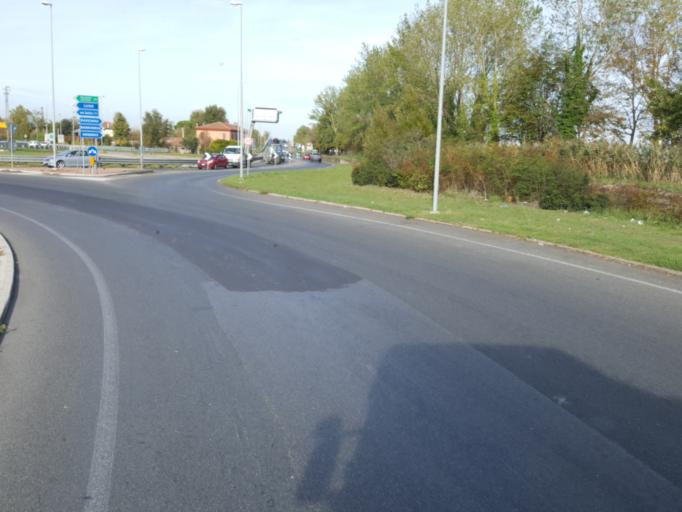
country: IT
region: Emilia-Romagna
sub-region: Provincia di Ravenna
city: Faenza
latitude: 44.3195
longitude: 11.9037
